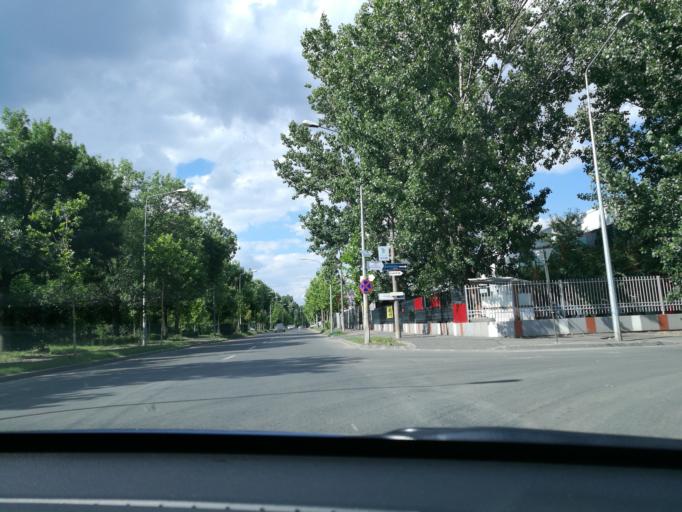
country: RO
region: Ilfov
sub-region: Comuna Glina
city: Catelu
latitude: 44.4209
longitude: 26.2190
